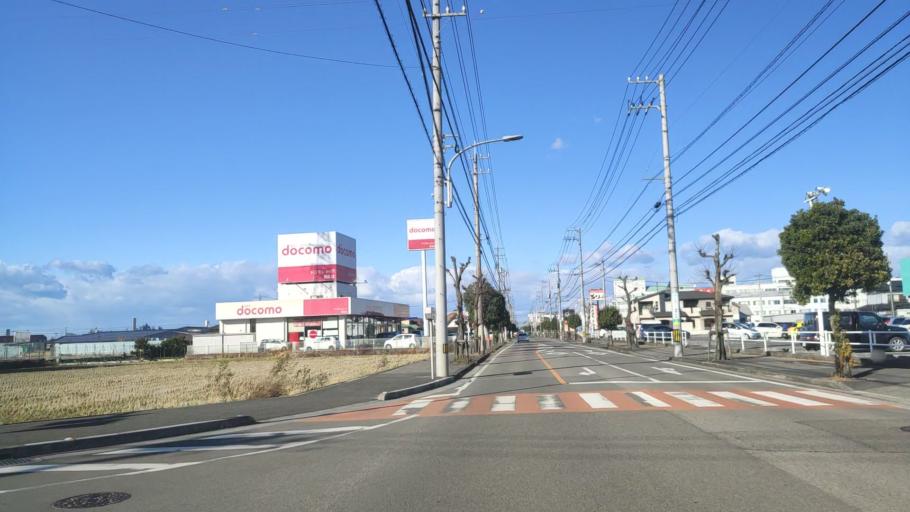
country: JP
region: Ehime
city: Saijo
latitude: 33.9255
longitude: 133.1909
